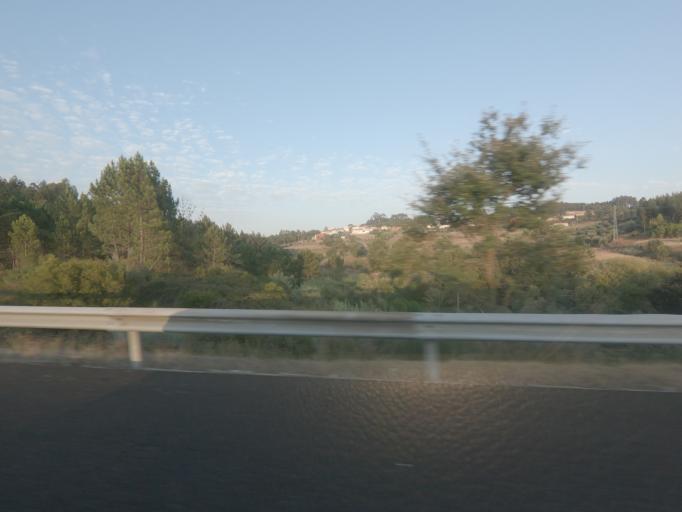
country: PT
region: Leiria
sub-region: Leiria
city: Caranguejeira
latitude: 39.7728
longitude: -8.7438
